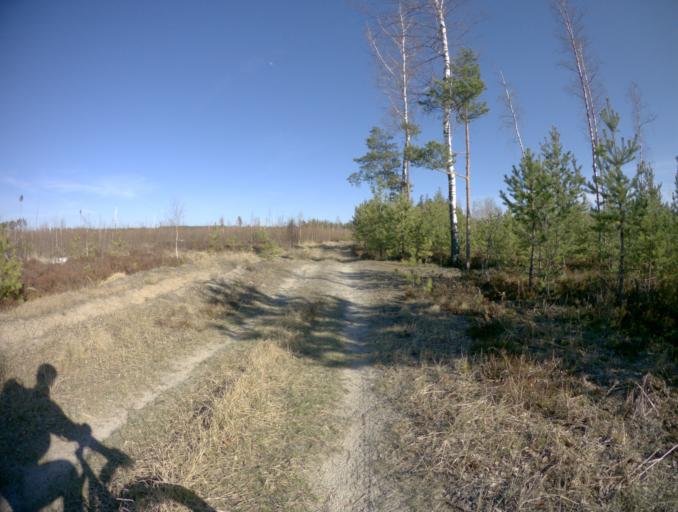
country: RU
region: Vladimir
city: Ivanishchi
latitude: 55.7060
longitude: 40.4383
